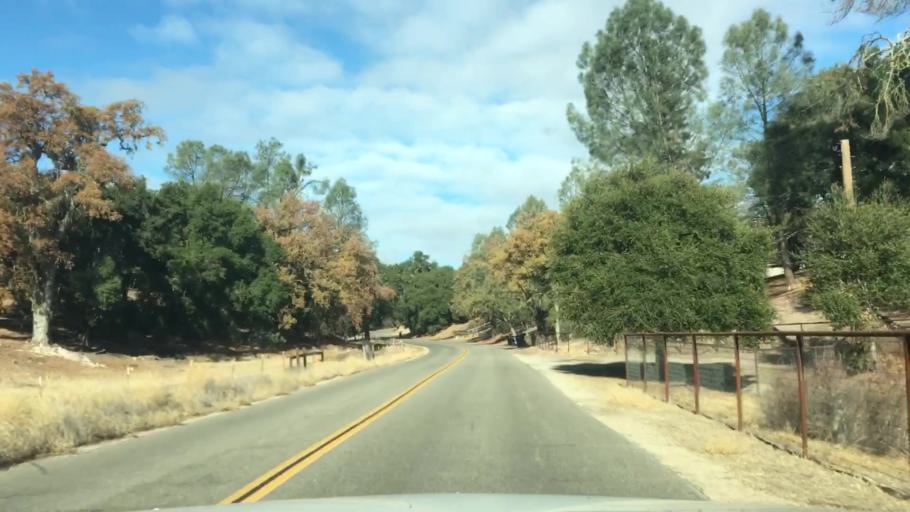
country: US
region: California
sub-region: San Luis Obispo County
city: Atascadero
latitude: 35.4502
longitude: -120.6518
